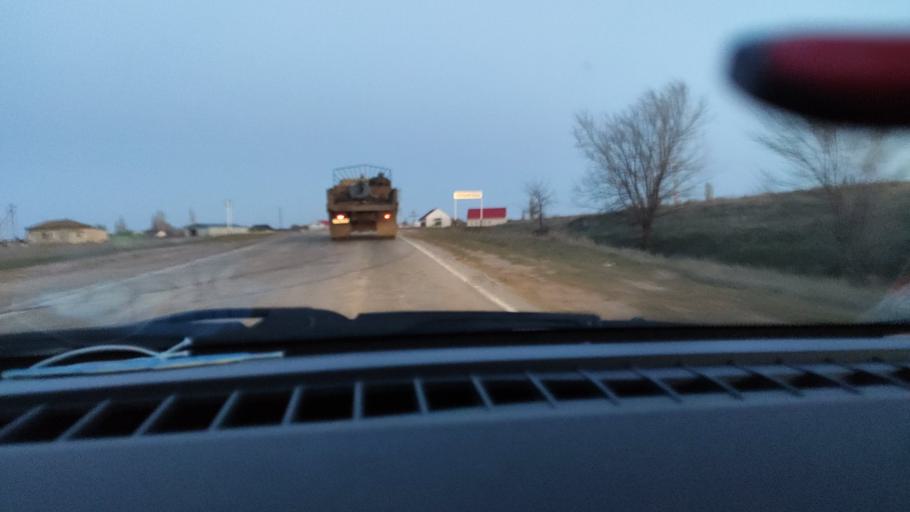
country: RU
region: Saratov
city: Rovnoye
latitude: 51.0260
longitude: 46.0928
